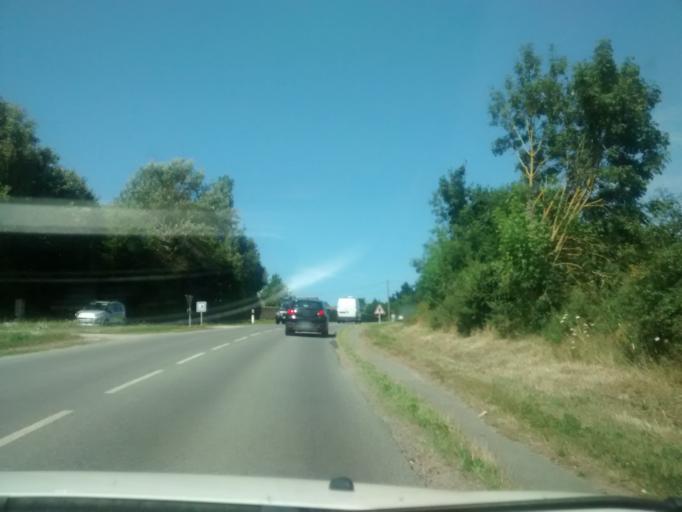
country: FR
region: Brittany
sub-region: Departement d'Ille-et-Vilaine
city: Cancale
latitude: 48.6948
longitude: -1.8525
